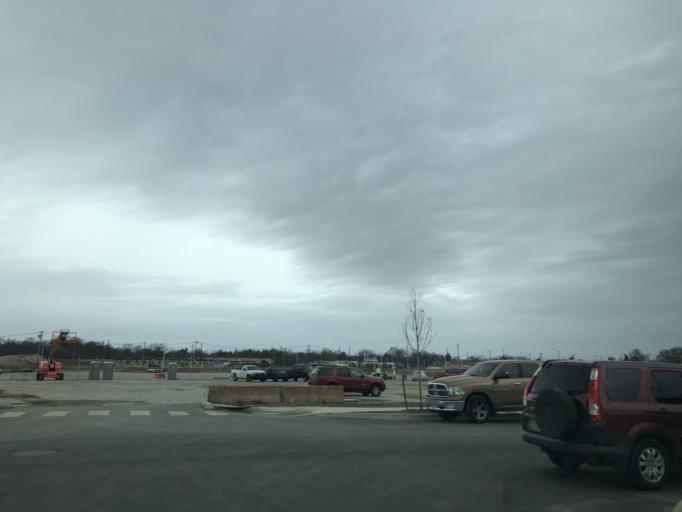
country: US
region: Delaware
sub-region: New Castle County
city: Newark
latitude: 39.6638
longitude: -75.7572
